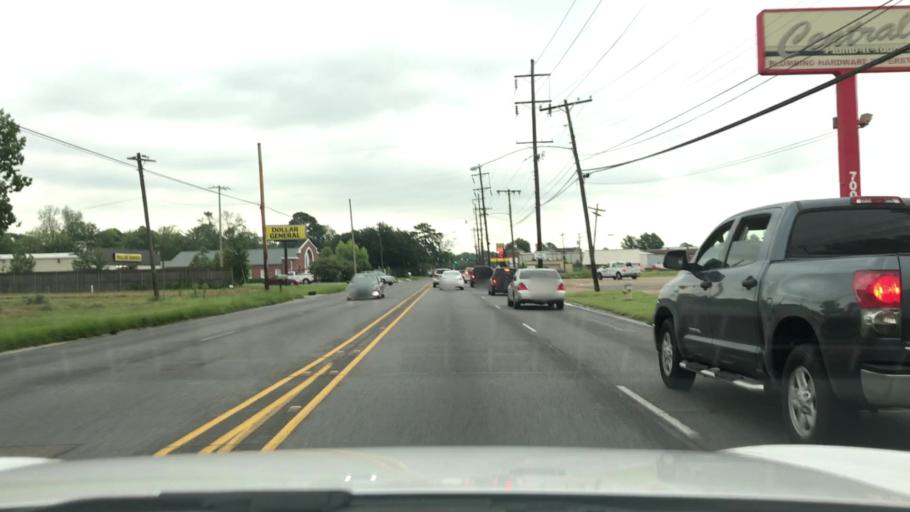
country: US
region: Louisiana
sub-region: East Baton Rouge Parish
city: Merrydale
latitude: 30.4732
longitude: -91.1203
